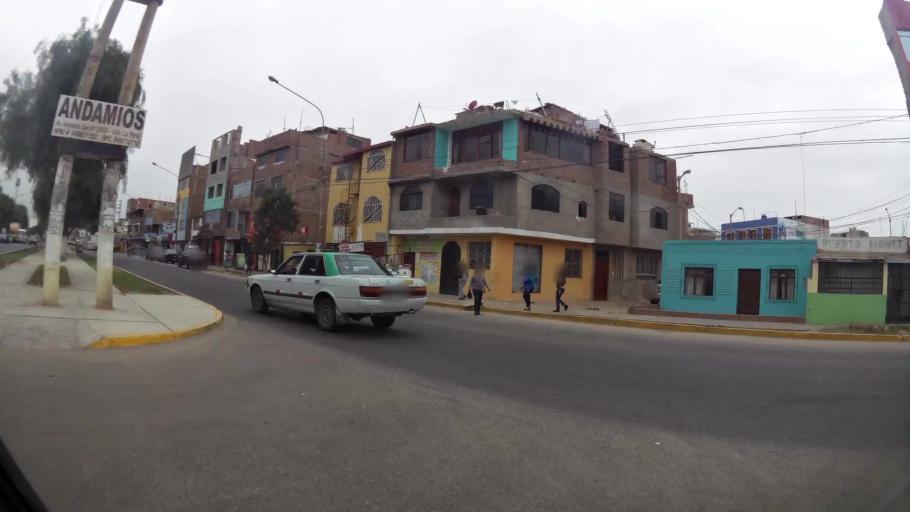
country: PE
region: La Libertad
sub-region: Provincia de Trujillo
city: Trujillo
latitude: -8.1265
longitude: -79.0293
